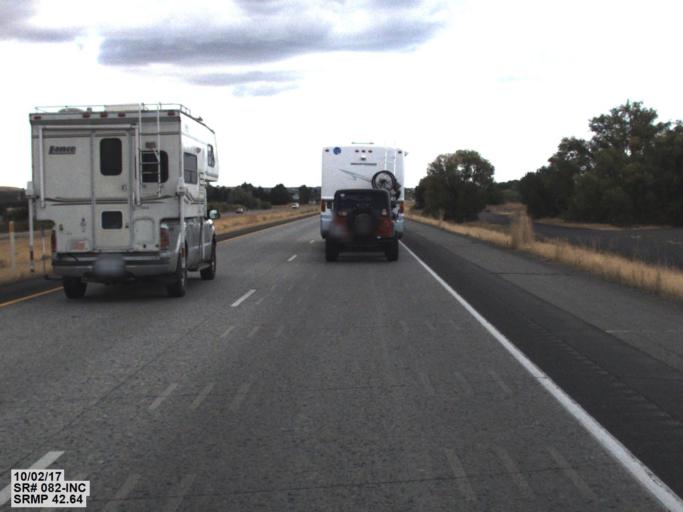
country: US
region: Washington
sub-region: Yakima County
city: Wapato
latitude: 46.4885
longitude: -120.4205
